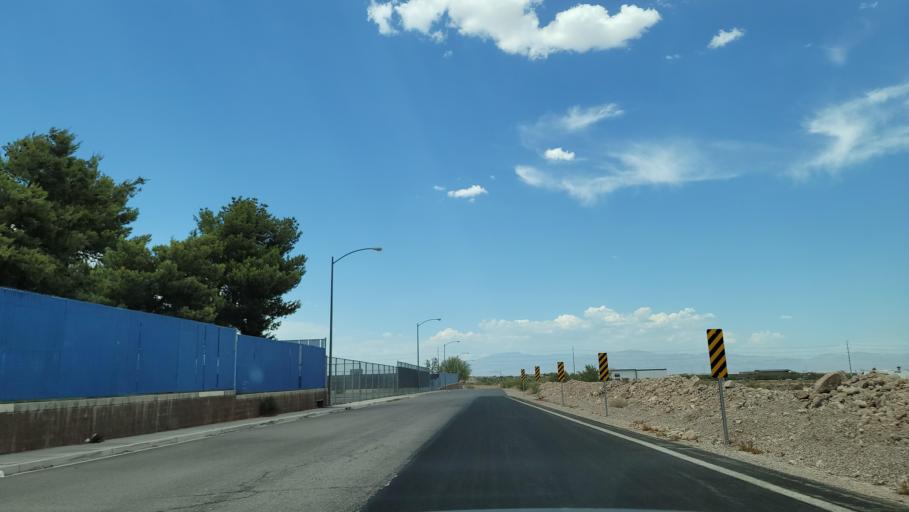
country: US
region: Nevada
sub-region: Clark County
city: Enterprise
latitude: 36.0495
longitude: -115.2656
